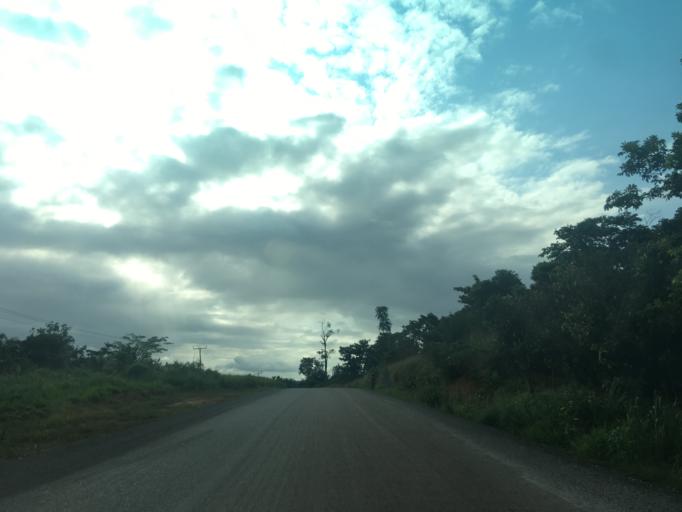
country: GH
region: Western
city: Bibiani
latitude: 6.1180
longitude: -2.3268
